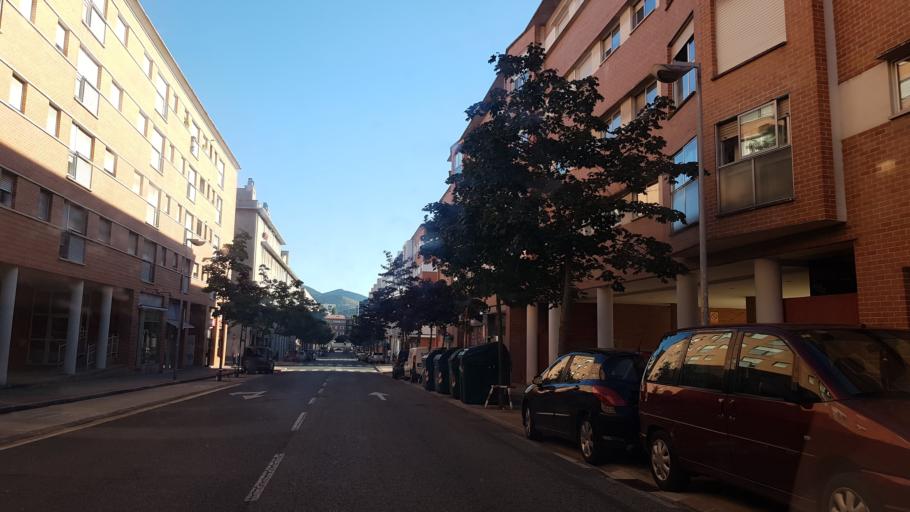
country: ES
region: Navarre
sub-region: Provincia de Navarra
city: Burlata
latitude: 42.8108
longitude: -1.6111
